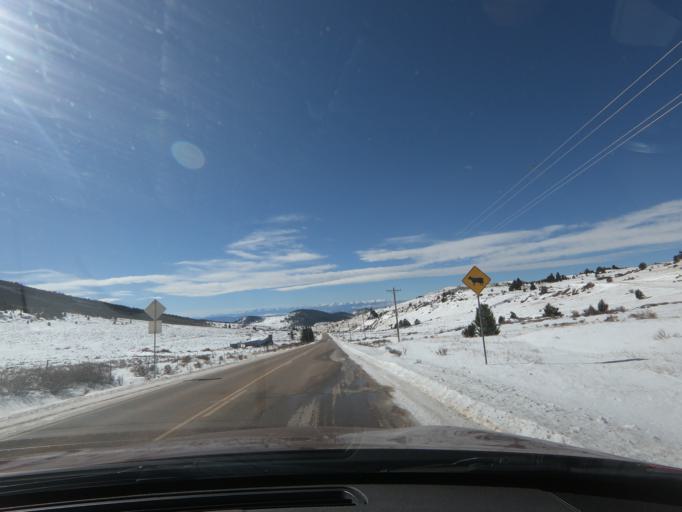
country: US
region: Colorado
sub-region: Teller County
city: Cripple Creek
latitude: 38.7281
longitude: -105.1198
